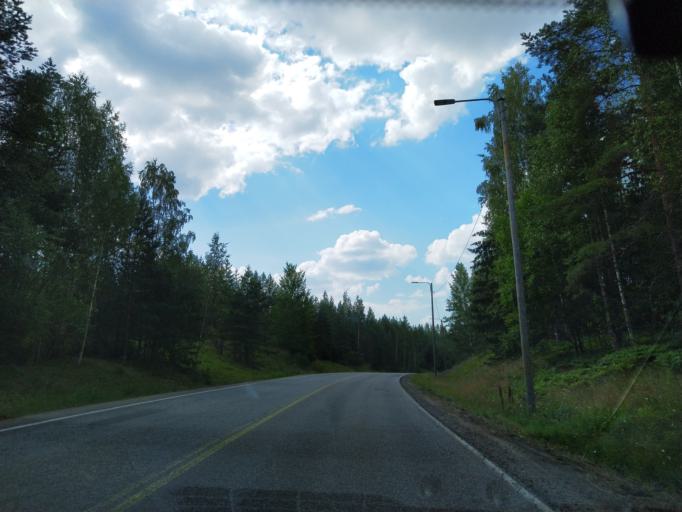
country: FI
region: Uusimaa
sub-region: Helsinki
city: Kirkkonummi
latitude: 60.1089
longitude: 24.4832
